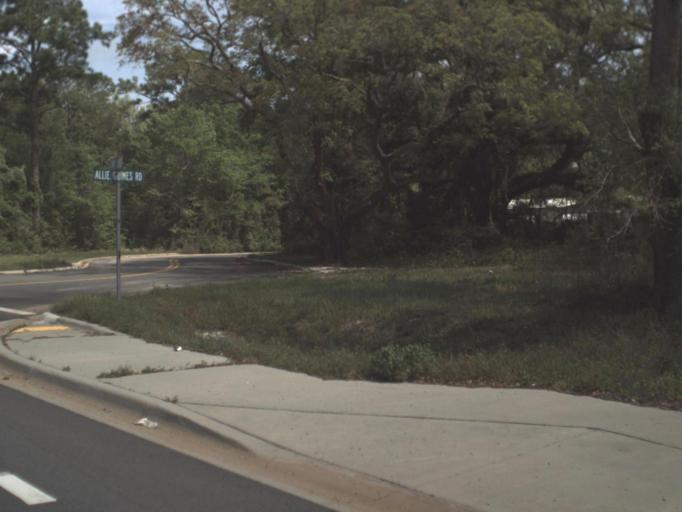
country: US
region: Florida
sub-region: Santa Rosa County
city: Holley
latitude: 30.4525
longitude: -86.9074
